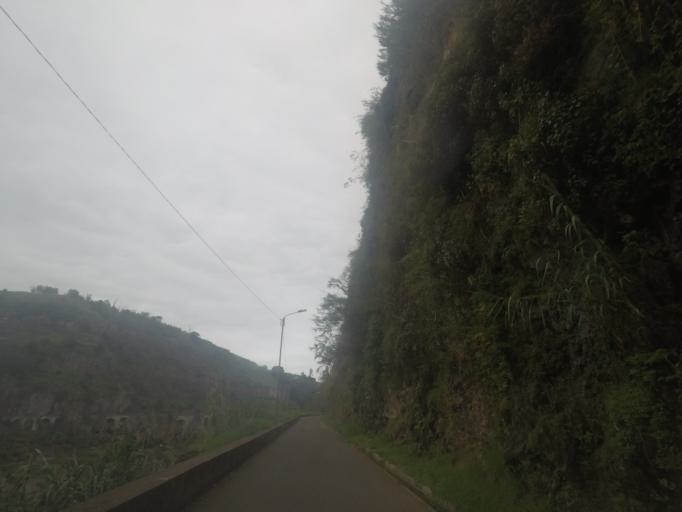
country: PT
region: Madeira
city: Camara de Lobos
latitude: 32.6622
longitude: -16.9623
